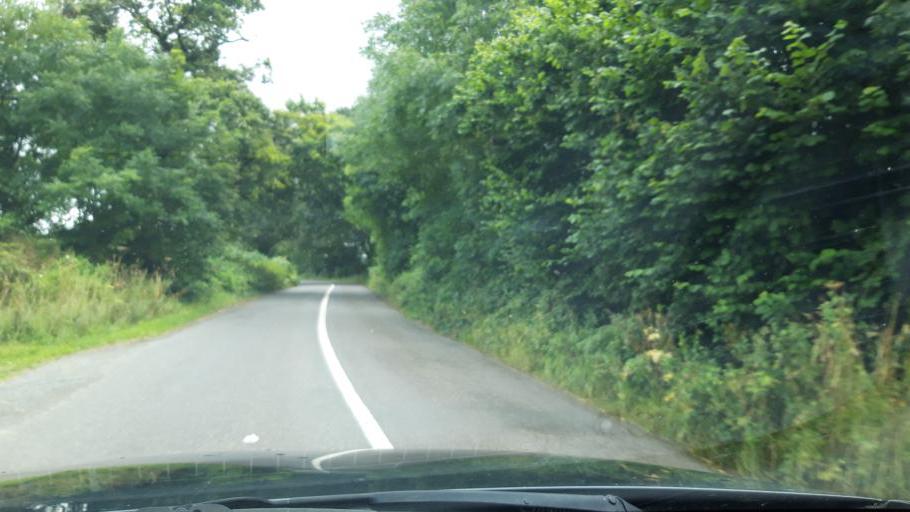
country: IE
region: Munster
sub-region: County Cork
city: Castlemartyr
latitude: 52.1312
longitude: -7.9919
